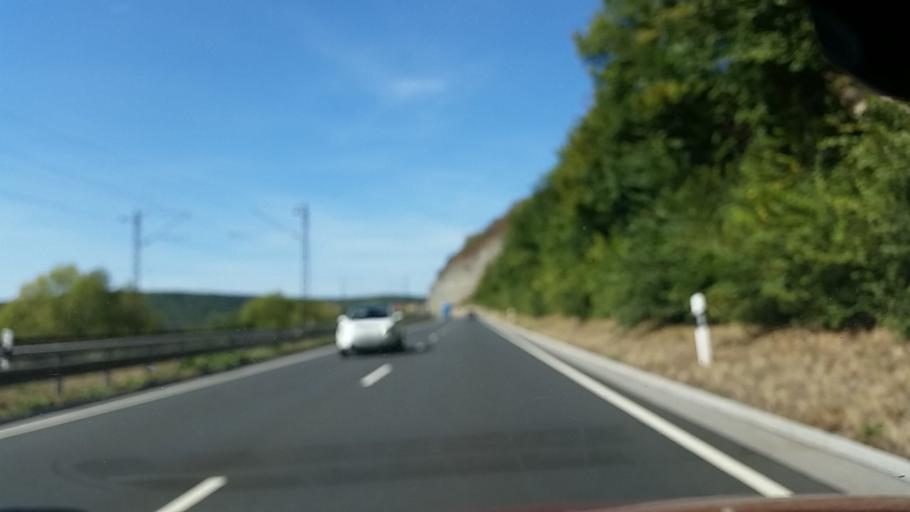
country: DE
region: Bavaria
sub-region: Regierungsbezirk Unterfranken
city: Zellingen
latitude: 49.8987
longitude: 9.8281
